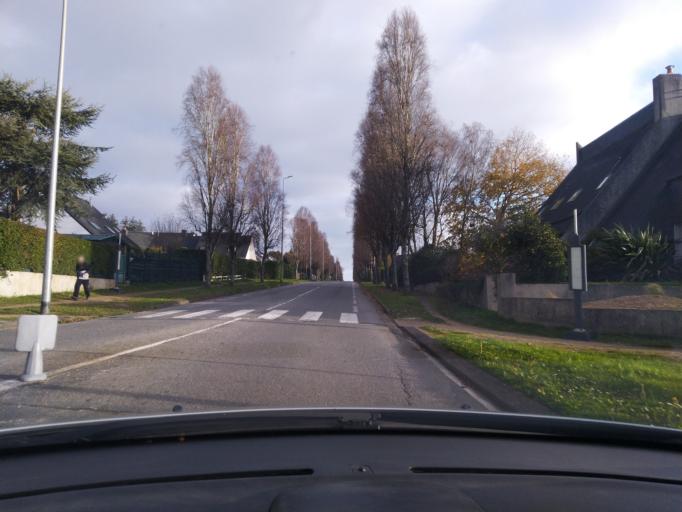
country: FR
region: Brittany
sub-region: Departement du Finistere
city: Morlaix
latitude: 48.5840
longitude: -3.8161
